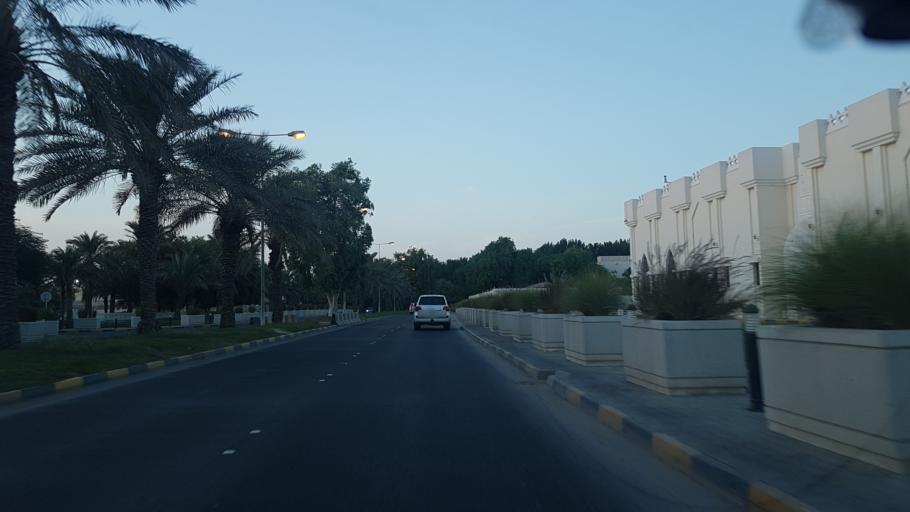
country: BH
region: Northern
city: Ar Rifa'
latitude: 26.1225
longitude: 50.5359
